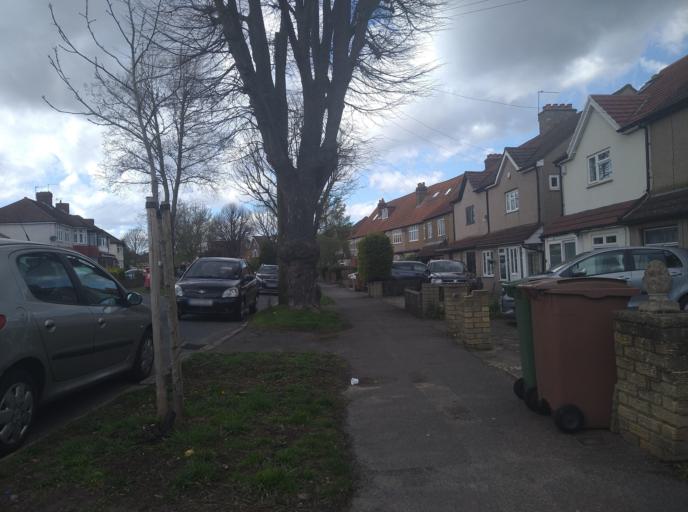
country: GB
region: England
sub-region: Greater London
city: Carshalton
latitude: 51.3721
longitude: -0.1841
